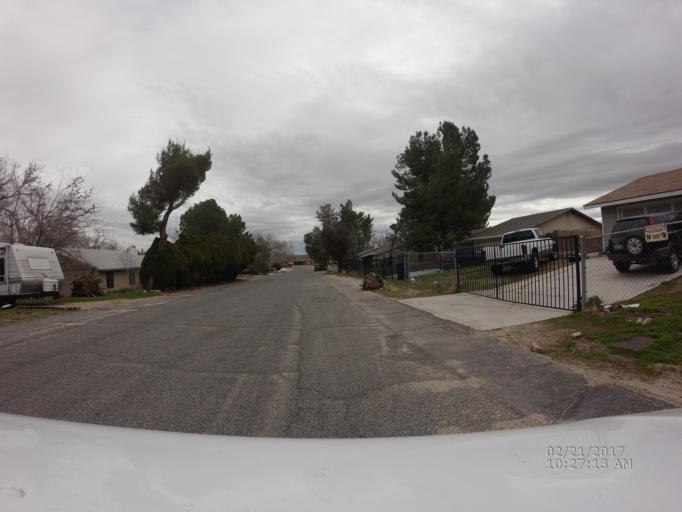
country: US
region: California
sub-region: Los Angeles County
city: Lake Los Angeles
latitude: 34.6070
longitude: -117.8122
